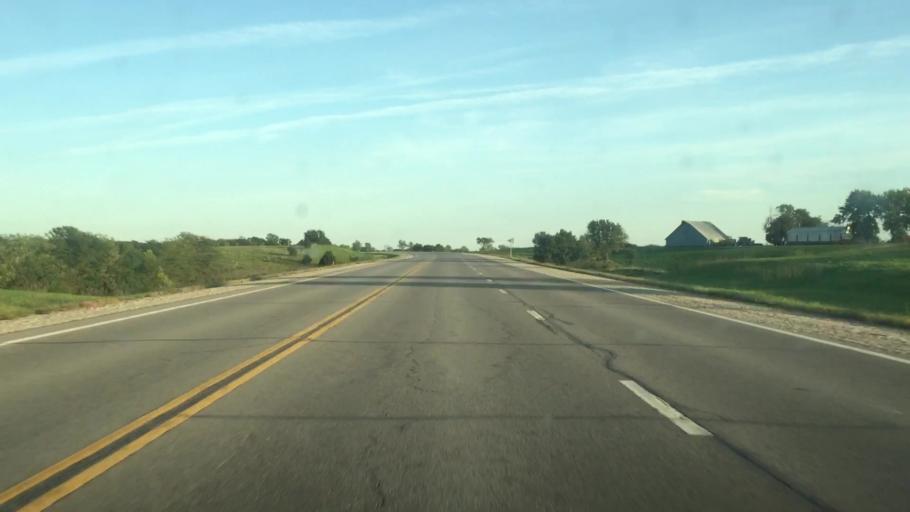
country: US
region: Kansas
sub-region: Atchison County
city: Atchison
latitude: 39.4761
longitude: -95.1036
